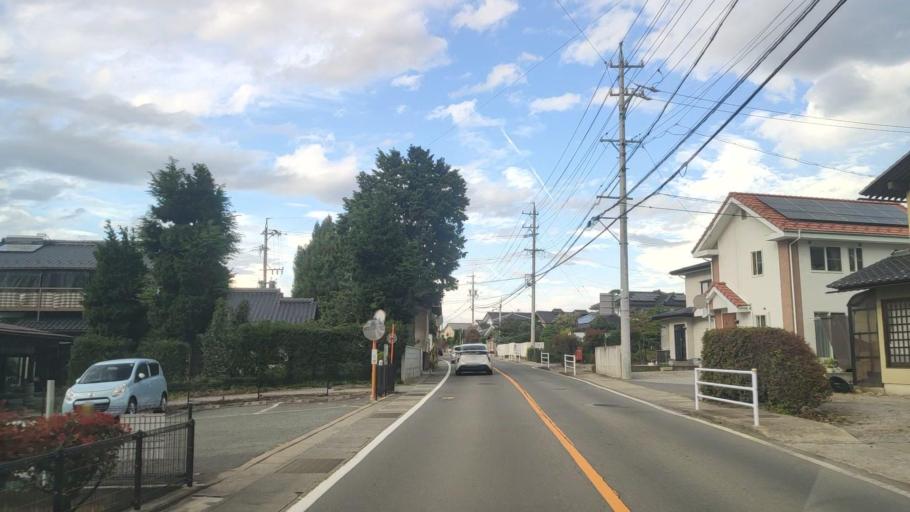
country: JP
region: Nagano
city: Suzaka
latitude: 36.6635
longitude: 138.3152
